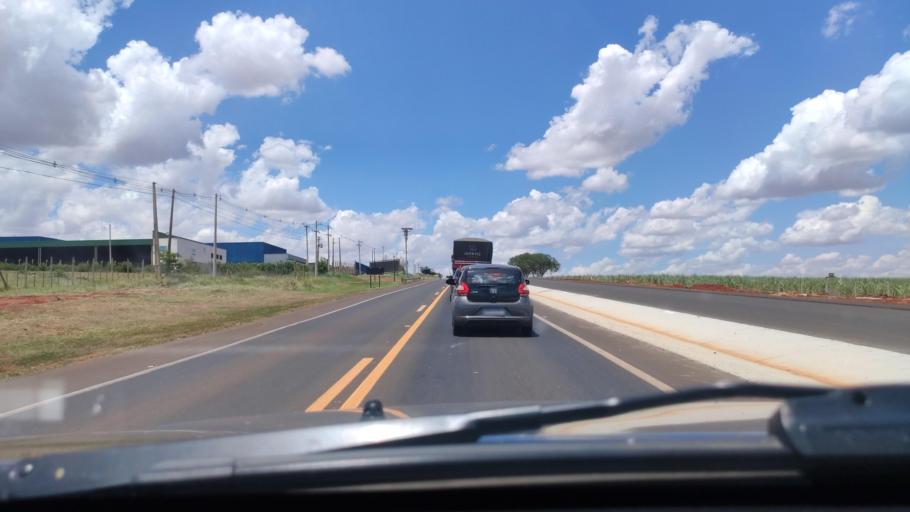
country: BR
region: Sao Paulo
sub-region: Jau
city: Jau
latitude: -22.2415
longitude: -48.5399
